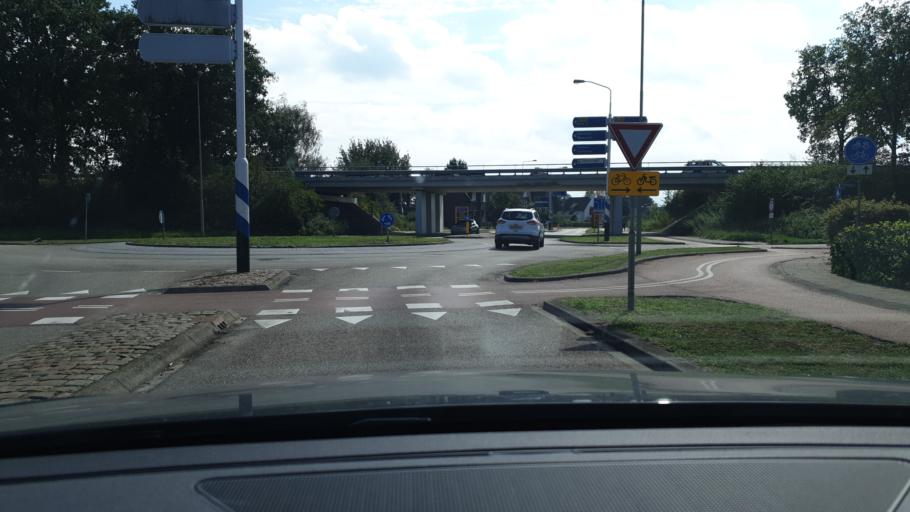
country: NL
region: Limburg
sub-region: Gemeente Venray
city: Venray
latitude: 51.5160
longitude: 5.9805
